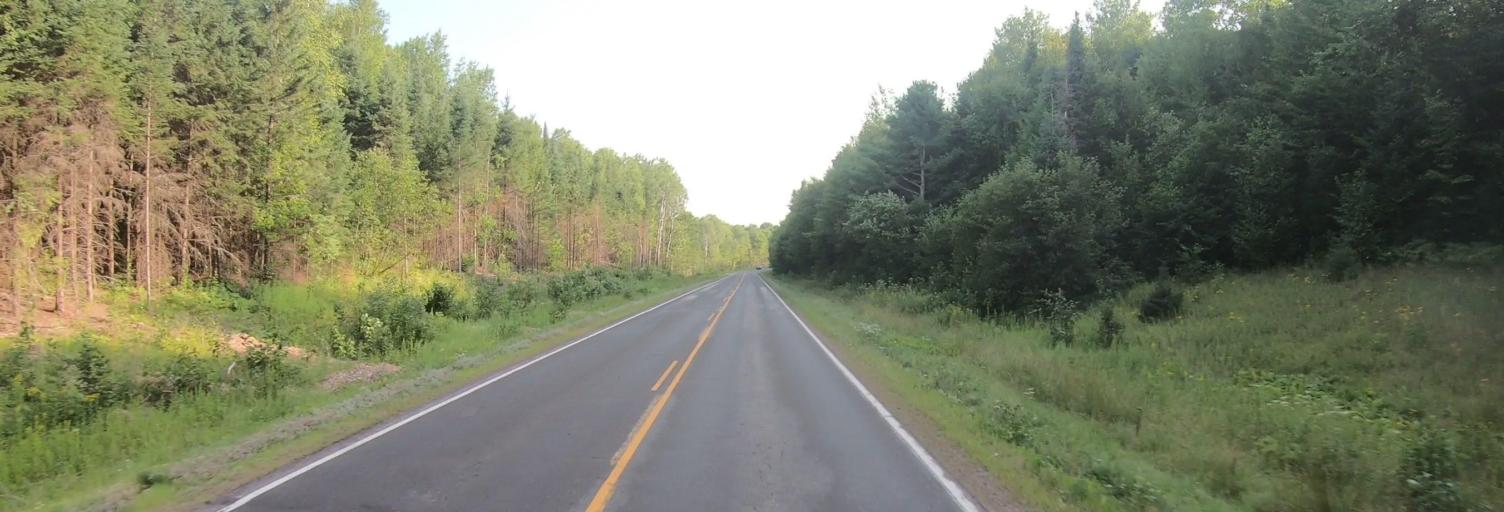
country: US
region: Wisconsin
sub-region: Ashland County
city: Ashland
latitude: 46.2871
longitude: -90.8250
